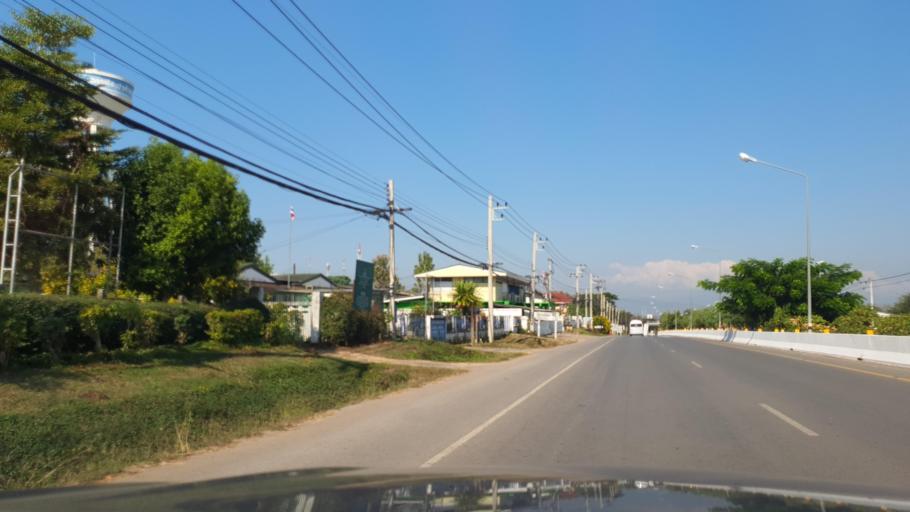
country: TH
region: Nan
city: Pua
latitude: 19.1731
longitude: 100.9186
